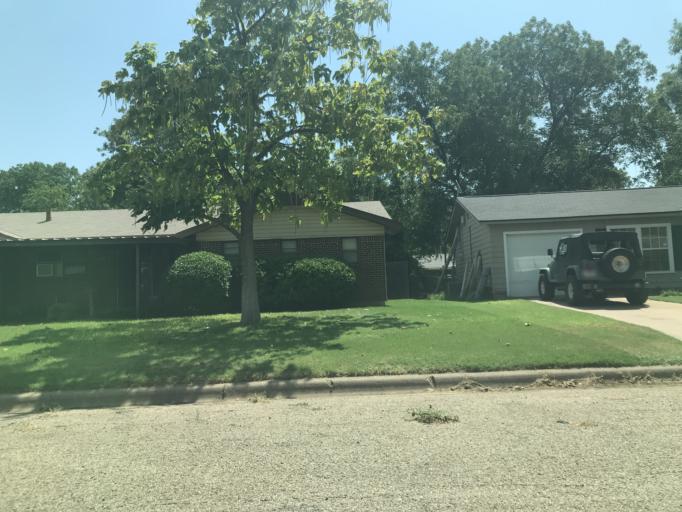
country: US
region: Texas
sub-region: Taylor County
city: Abilene
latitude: 32.4722
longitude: -99.7674
